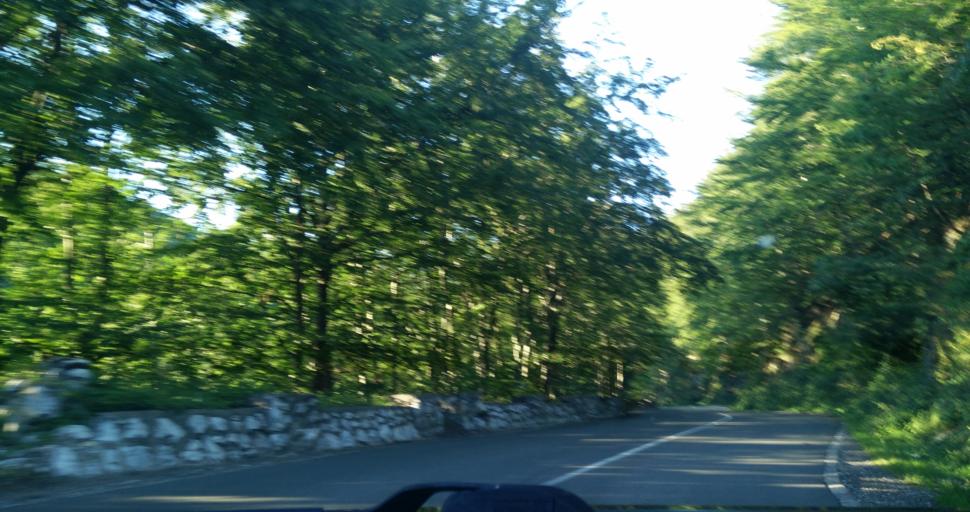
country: RO
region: Bihor
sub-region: Oras Nucet
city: Nucet
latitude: 46.4818
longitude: 22.5966
